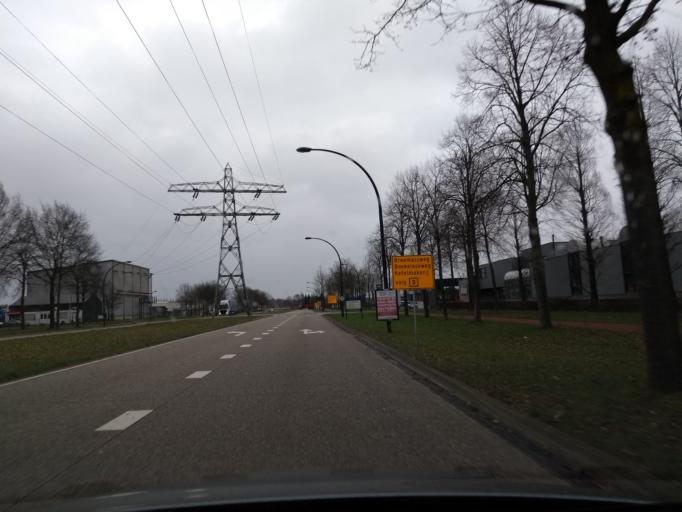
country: NL
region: Overijssel
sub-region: Gemeente Hengelo
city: Hengelo
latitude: 52.2405
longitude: 6.7816
